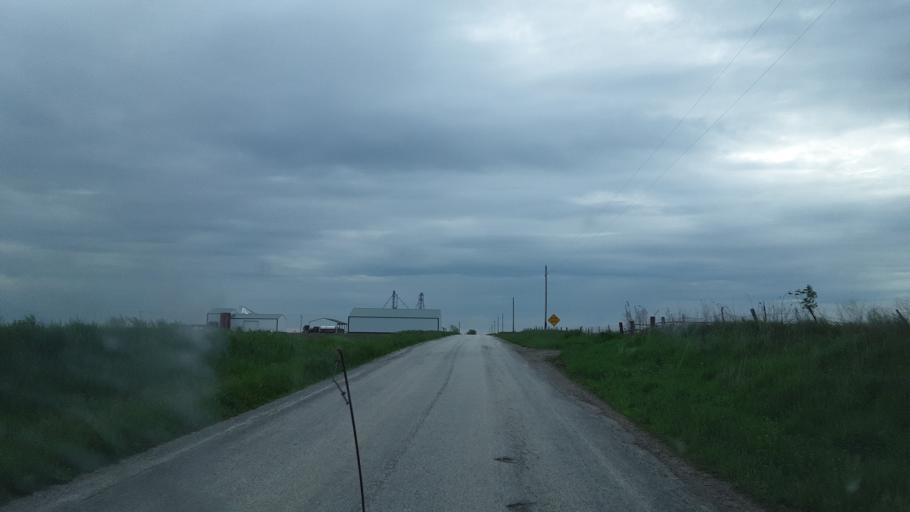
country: US
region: Illinois
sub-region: McDonough County
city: Macomb
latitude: 40.3816
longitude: -90.6237
